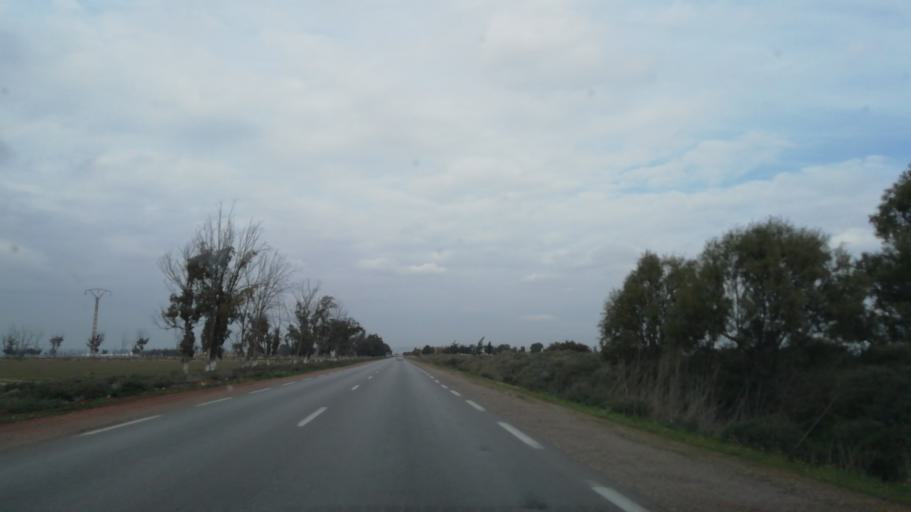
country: DZ
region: Mostaganem
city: Mostaganem
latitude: 35.6780
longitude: 0.0572
